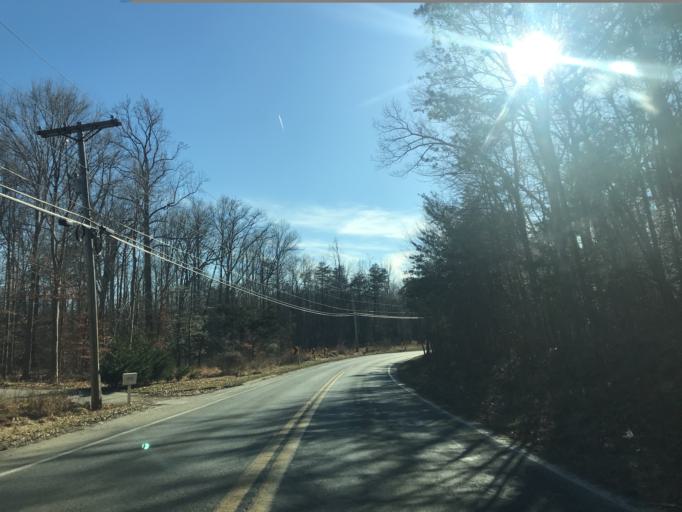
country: US
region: Maryland
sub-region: Prince George's County
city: Brandywine
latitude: 38.6944
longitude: -76.8870
